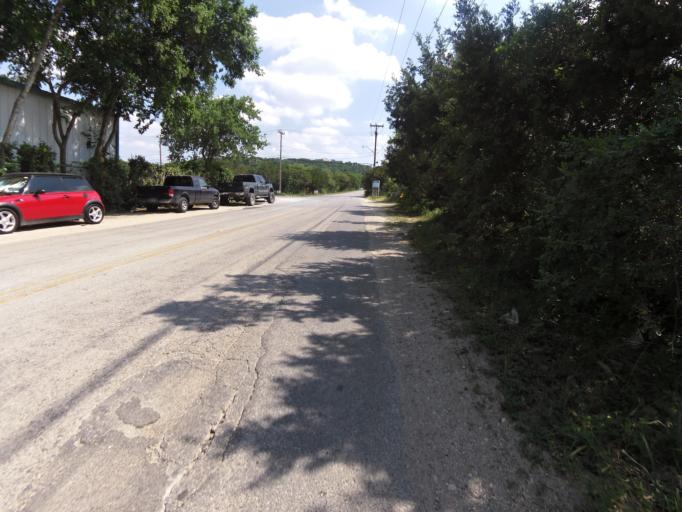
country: US
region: Texas
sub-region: Bexar County
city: Cross Mountain
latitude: 29.6372
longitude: -98.6248
